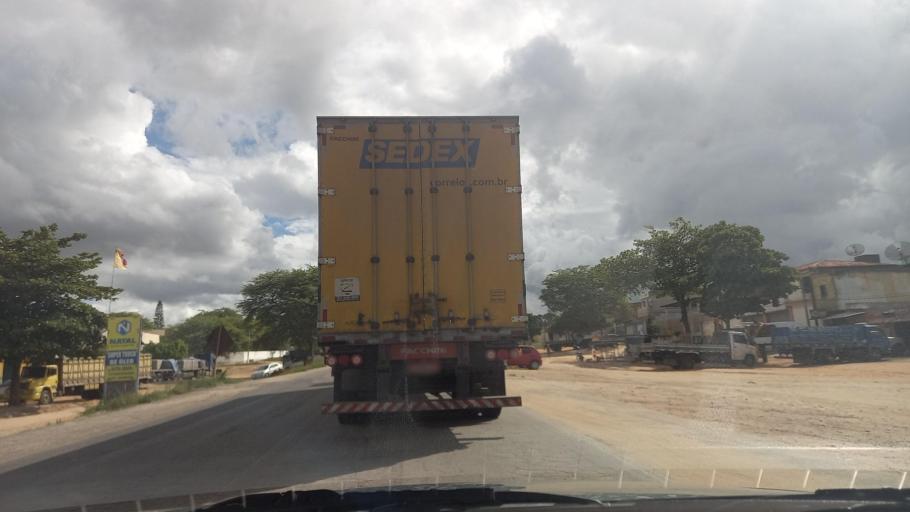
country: BR
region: Pernambuco
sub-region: Lajedo
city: Lajedo
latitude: -8.6574
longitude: -36.3259
